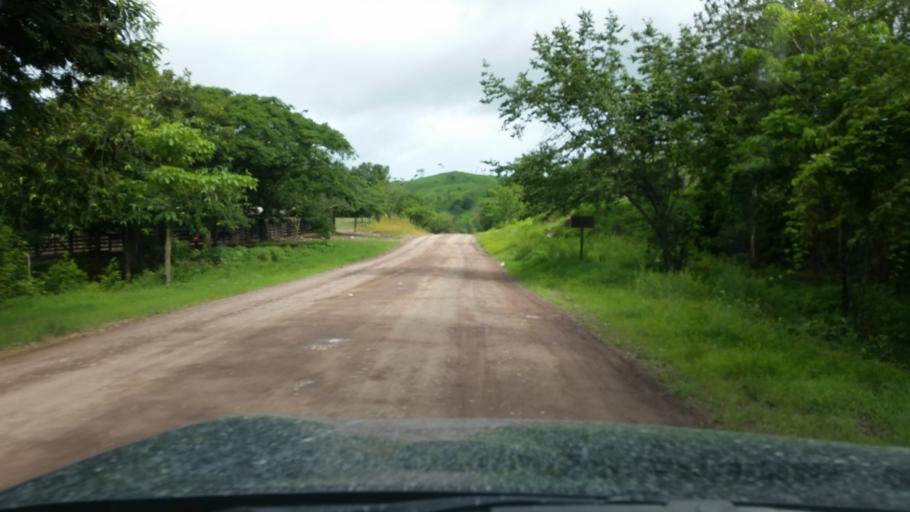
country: NI
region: Atlantico Norte (RAAN)
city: Siuna
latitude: 13.5309
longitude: -84.8233
